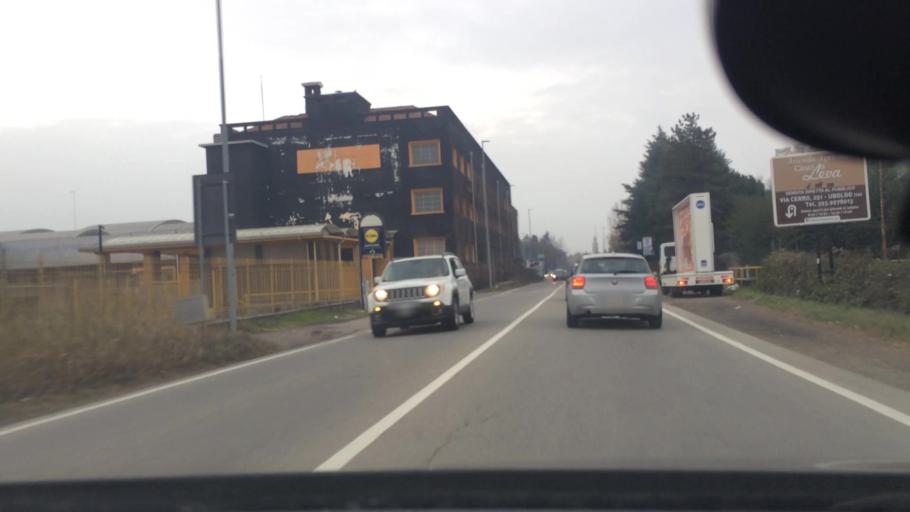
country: IT
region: Lombardy
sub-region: Provincia di Varese
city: Uboldo
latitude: 45.6201
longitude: 9.0147
